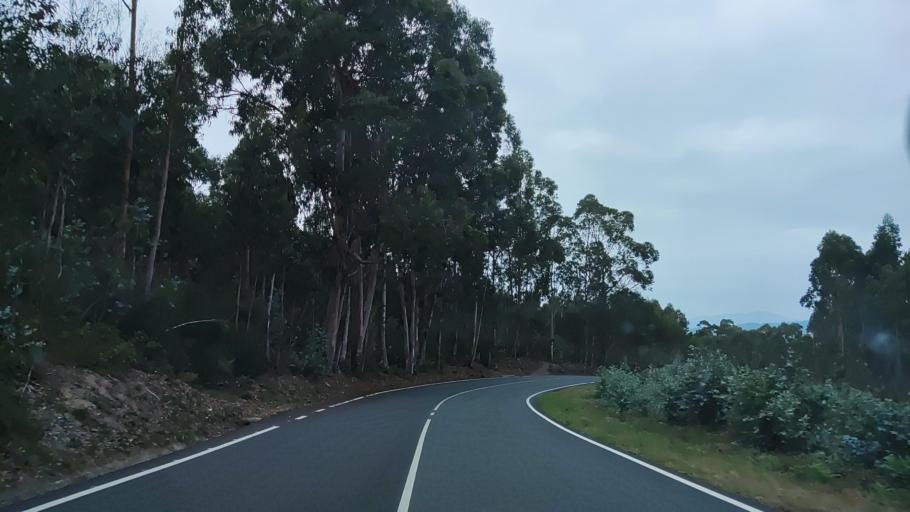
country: ES
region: Galicia
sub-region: Provincia de Pontevedra
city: Catoira
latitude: 42.6567
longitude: -8.7526
